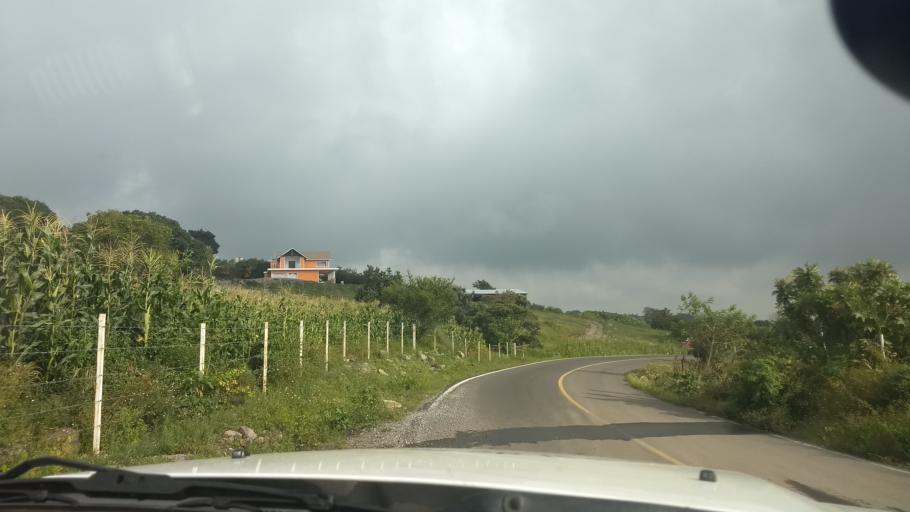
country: MX
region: Colima
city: Queseria
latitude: 19.4061
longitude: -103.6200
